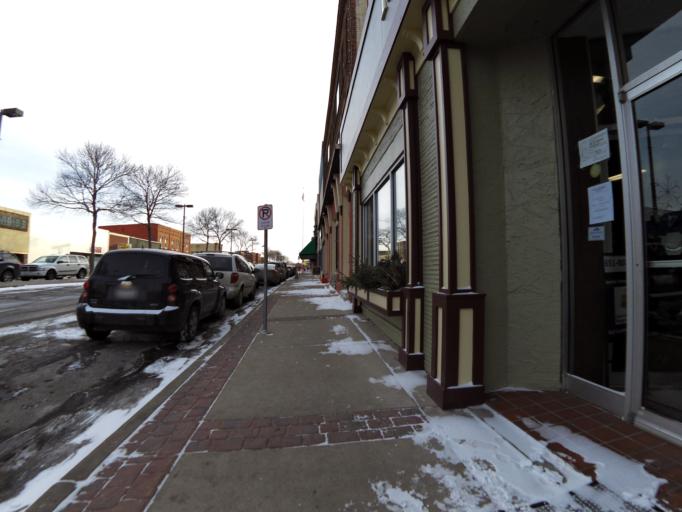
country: US
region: Wisconsin
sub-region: Pierce County
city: River Falls
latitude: 44.8595
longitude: -92.6258
